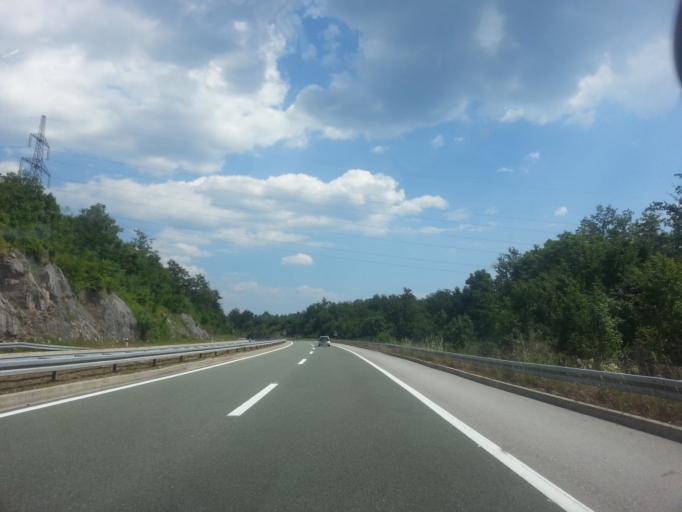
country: HR
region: Primorsko-Goranska
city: Matulji
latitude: 45.3832
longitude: 14.3039
